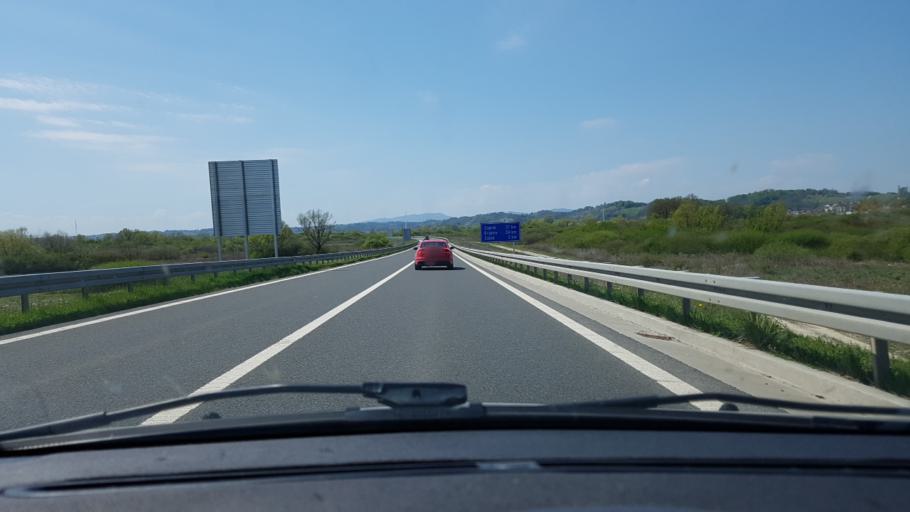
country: HR
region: Krapinsko-Zagorska
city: Zabok
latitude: 46.0144
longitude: 15.9267
